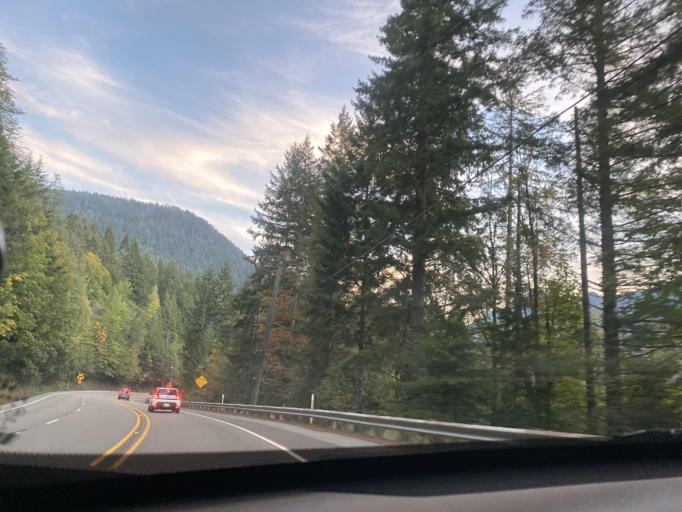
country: US
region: Washington
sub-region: Clallam County
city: Port Angeles
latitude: 48.0688
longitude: -123.5760
